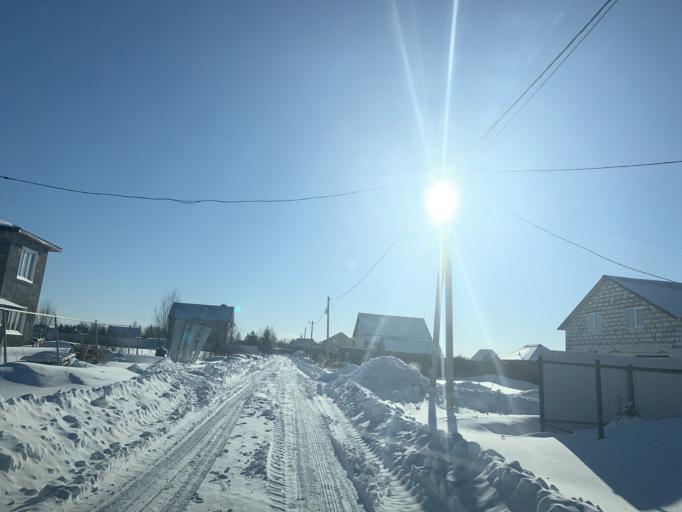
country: RU
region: Jaroslavl
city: Tunoshna
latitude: 57.6648
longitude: 40.0668
